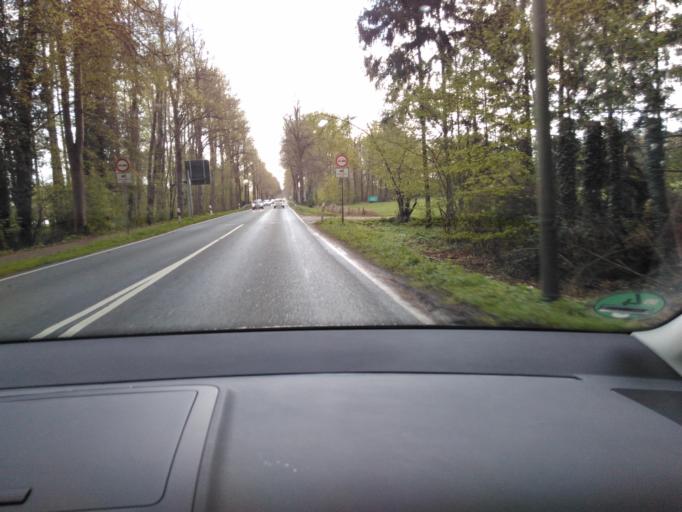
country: DE
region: North Rhine-Westphalia
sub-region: Regierungsbezirk Detmold
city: Steinhagen
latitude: 51.9445
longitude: 8.4294
